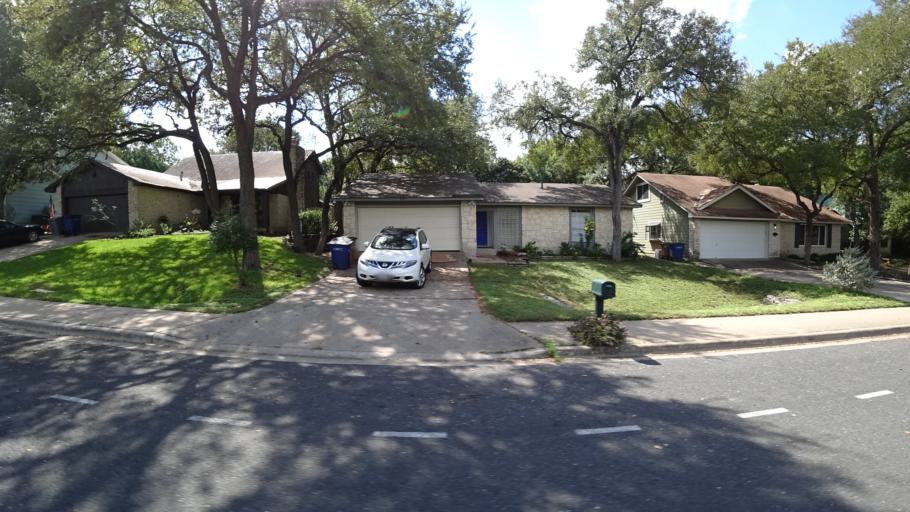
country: US
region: Texas
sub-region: Travis County
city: Onion Creek
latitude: 30.1832
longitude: -97.7904
